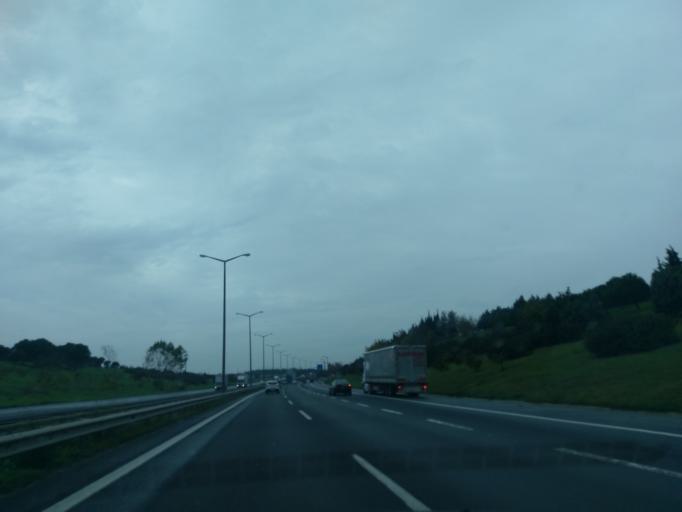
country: TR
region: Istanbul
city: Silivri
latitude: 41.1080
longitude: 28.2724
